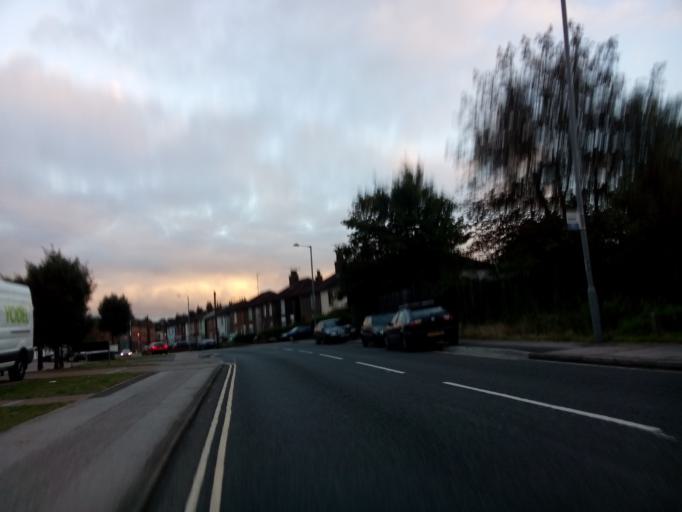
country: GB
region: England
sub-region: Suffolk
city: Ipswich
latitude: 52.0529
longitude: 1.1373
